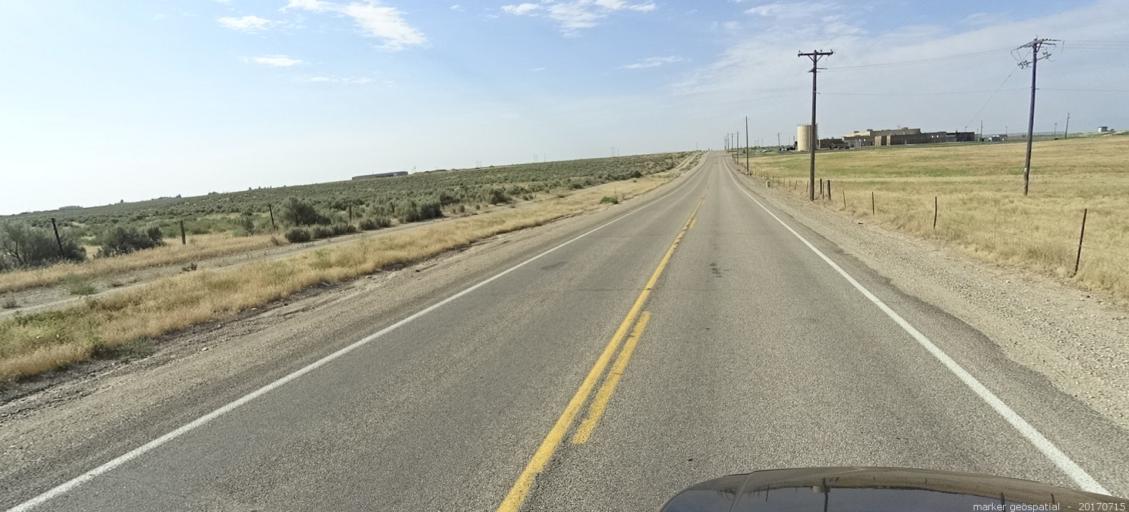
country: US
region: Idaho
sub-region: Ada County
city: Boise
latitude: 43.4651
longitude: -116.2344
